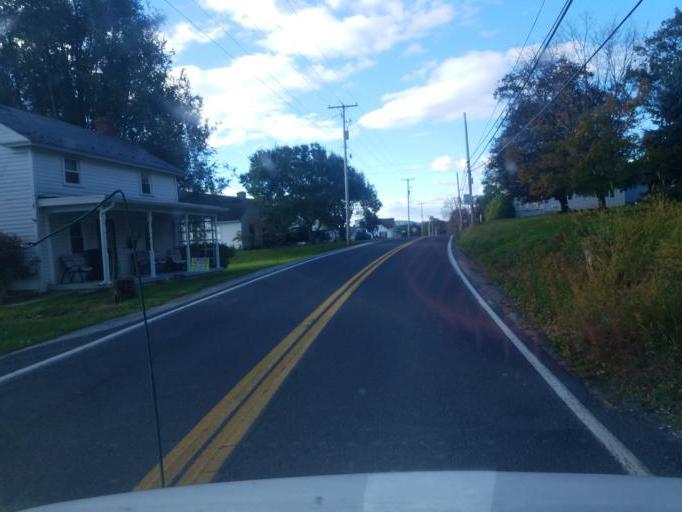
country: US
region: Pennsylvania
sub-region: Adams County
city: Biglerville
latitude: 39.8888
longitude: -77.3570
